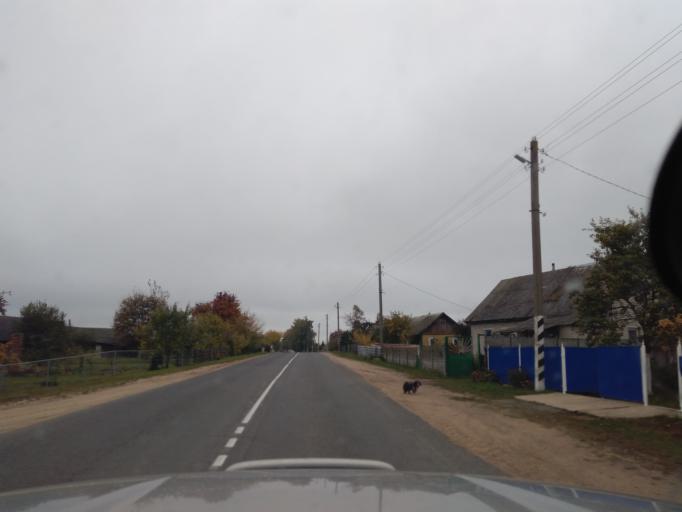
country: BY
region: Minsk
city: Kapyl'
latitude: 53.1517
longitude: 27.1491
